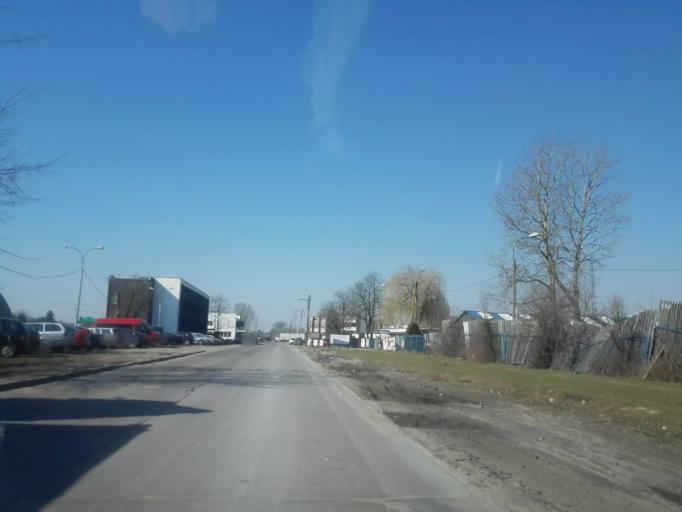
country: PL
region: Masovian Voivodeship
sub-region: Warszawa
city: Wilanow
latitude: 52.1819
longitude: 21.0883
